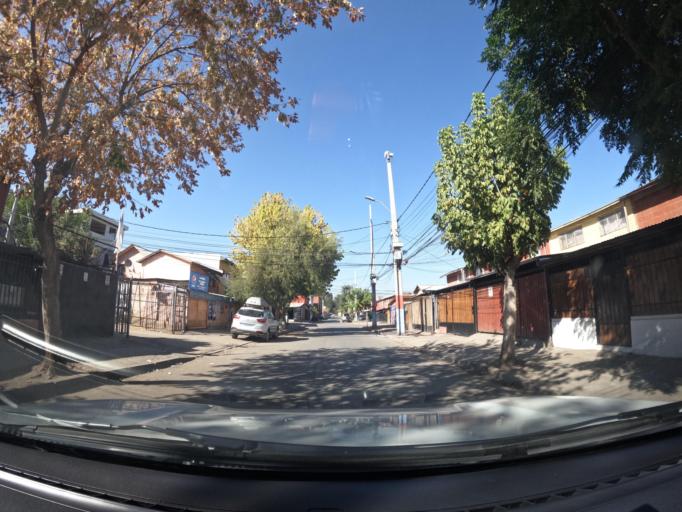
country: CL
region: Santiago Metropolitan
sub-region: Provincia de Santiago
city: Villa Presidente Frei, Nunoa, Santiago, Chile
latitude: -33.4802
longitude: -70.5691
